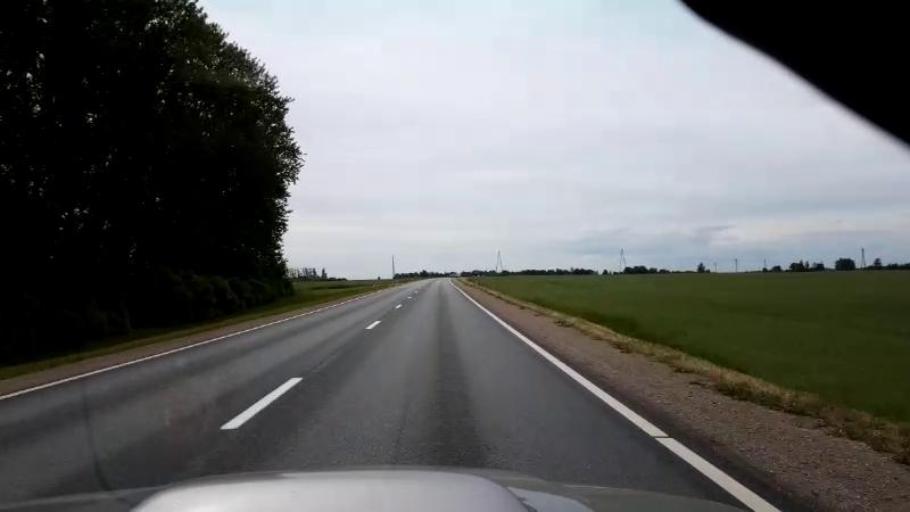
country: LV
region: Lecava
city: Iecava
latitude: 56.5407
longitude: 24.1731
